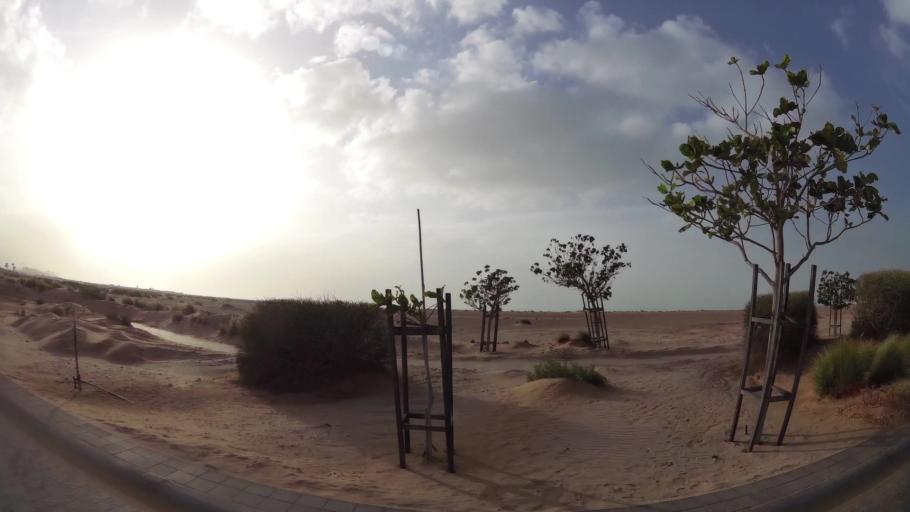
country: AE
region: Abu Dhabi
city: Abu Dhabi
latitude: 24.5554
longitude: 54.4498
